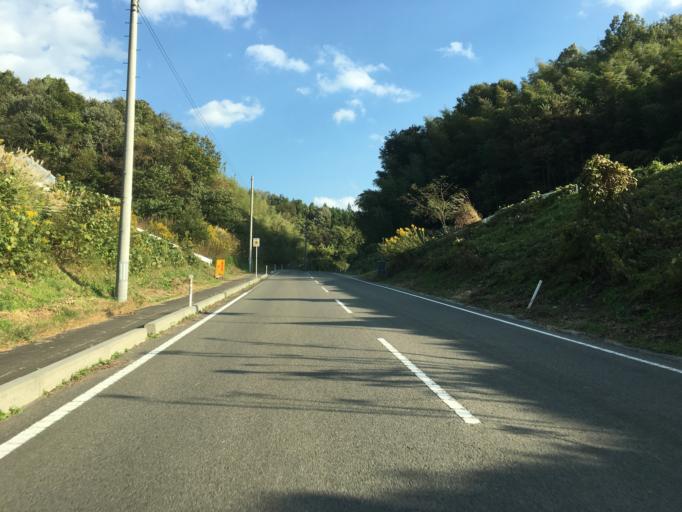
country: JP
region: Fukushima
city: Fukushima-shi
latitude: 37.6731
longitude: 140.5364
